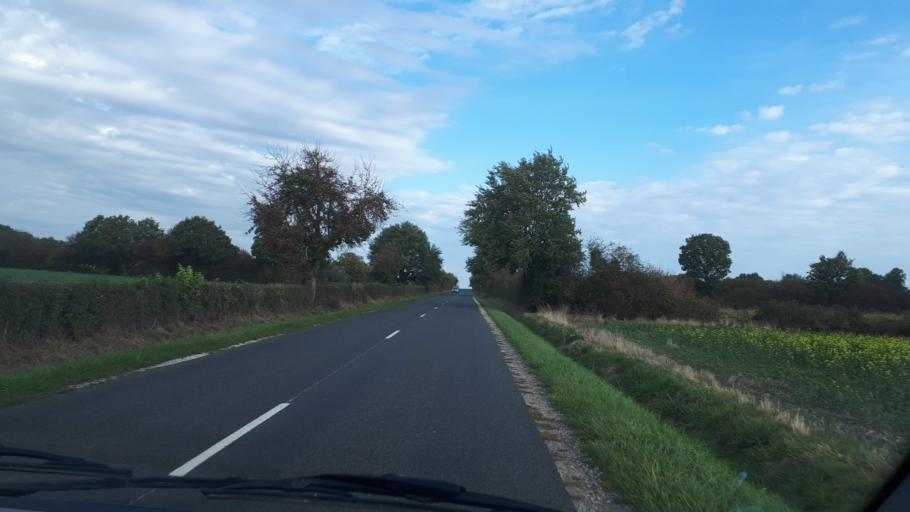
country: FR
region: Centre
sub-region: Departement du Loir-et-Cher
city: Mondoubleau
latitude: 47.9434
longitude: 0.9327
